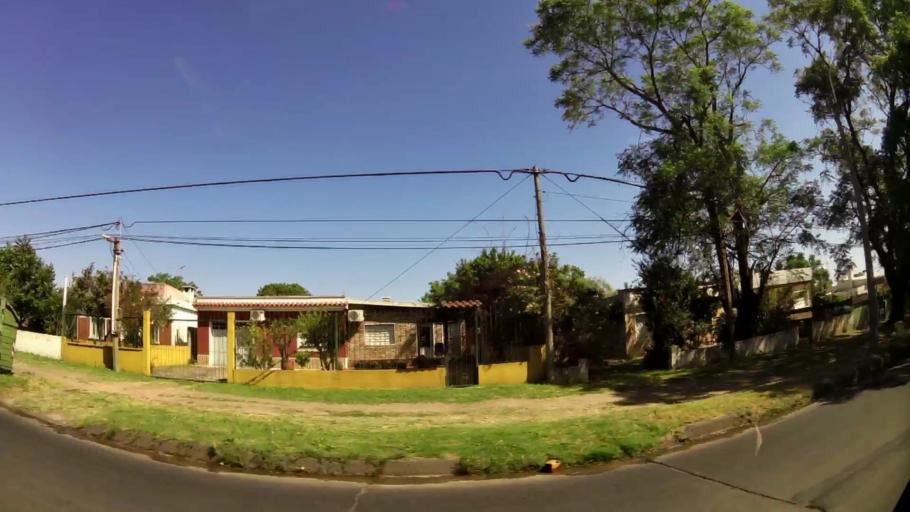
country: UY
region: Montevideo
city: Pajas Blancas
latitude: -34.8377
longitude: -56.2621
